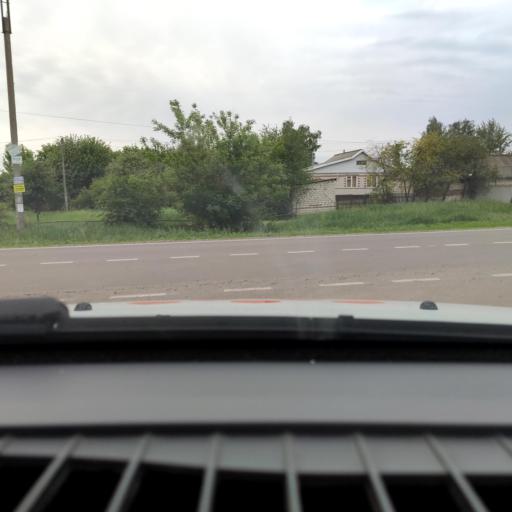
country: RU
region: Voronezj
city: Podkletnoye
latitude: 51.5924
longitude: 39.5251
